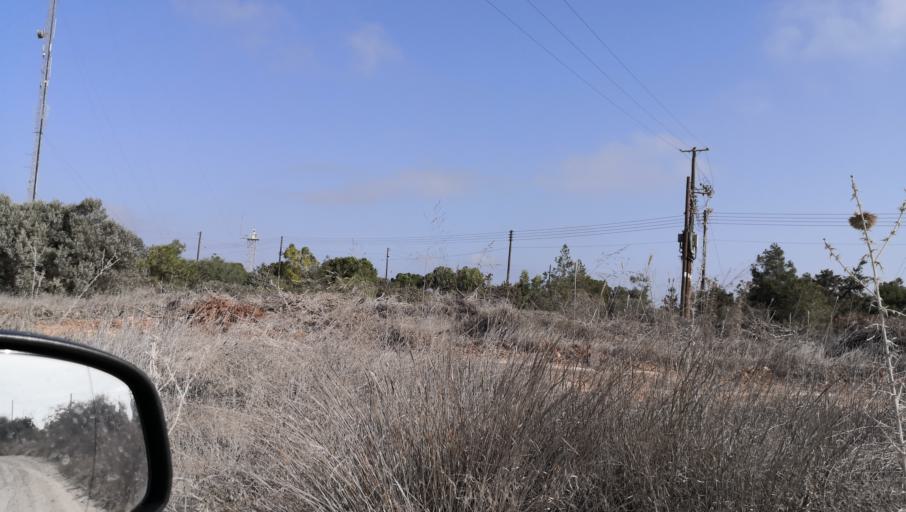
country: CY
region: Ammochostos
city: Protaras
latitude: 35.0038
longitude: 34.0302
